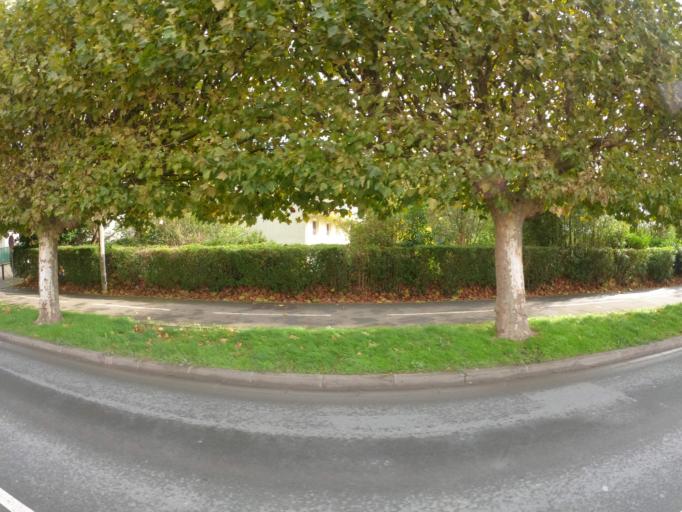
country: FR
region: Ile-de-France
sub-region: Departement de Seine-Saint-Denis
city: Montfermeil
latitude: 48.8971
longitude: 2.5906
